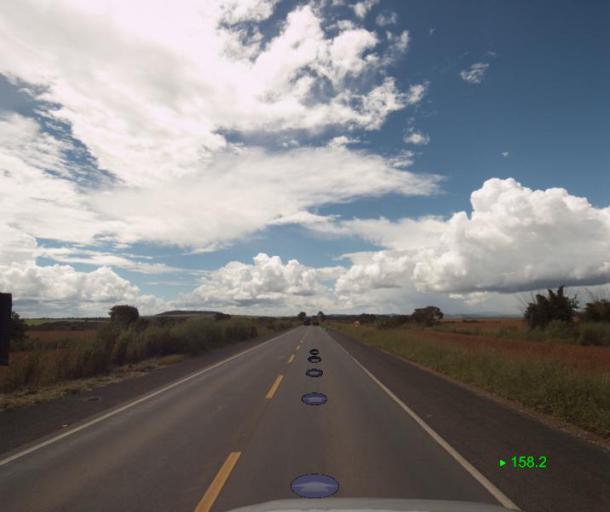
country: BR
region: Goias
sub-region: Uruacu
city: Uruacu
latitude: -14.1567
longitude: -49.1213
